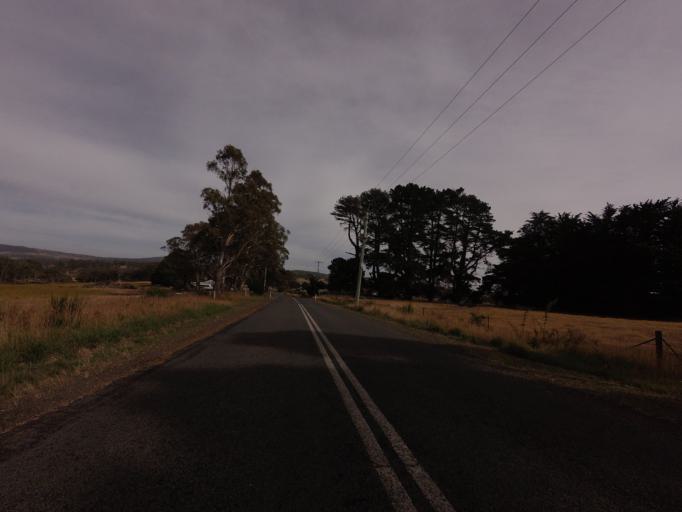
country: AU
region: Tasmania
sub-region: Brighton
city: Bridgewater
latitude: -42.3970
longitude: 147.4380
